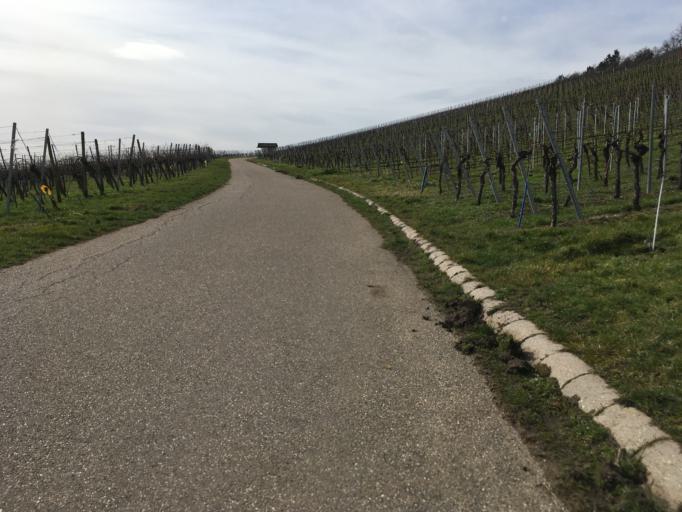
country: DE
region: Baden-Wuerttemberg
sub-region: Regierungsbezirk Stuttgart
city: Leingarten
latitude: 49.1290
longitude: 9.1125
